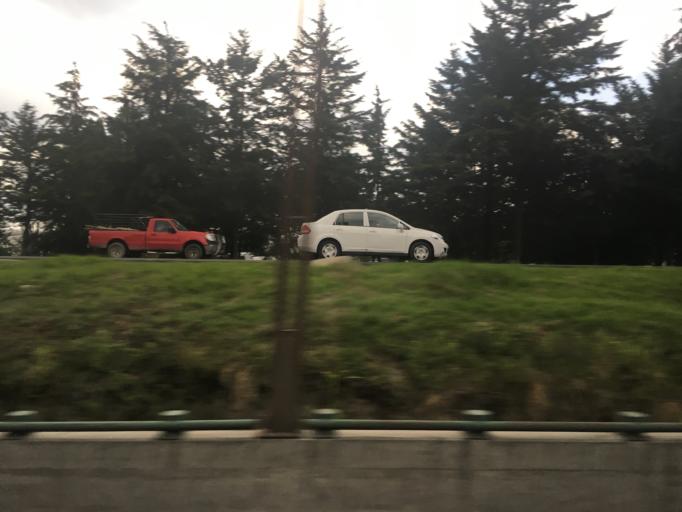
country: MX
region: Mexico
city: Santa Maria Totoltepec
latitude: 19.2870
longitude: -99.5961
